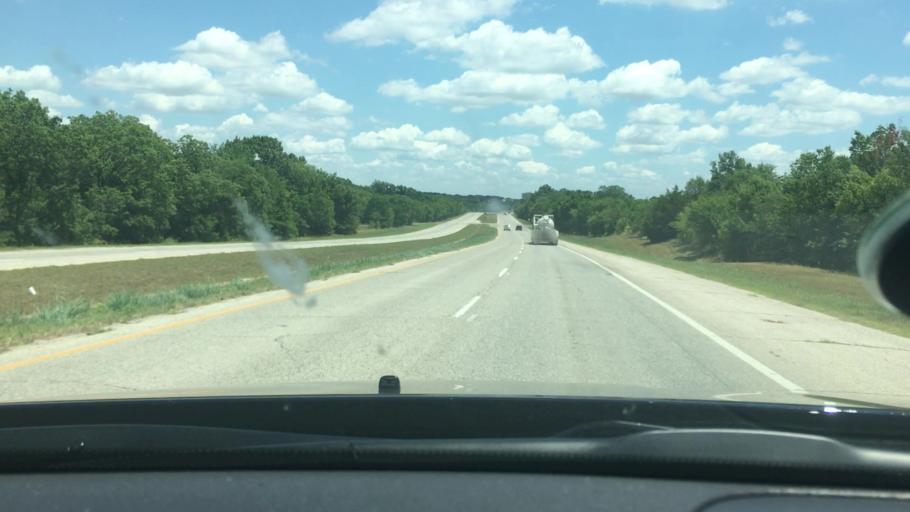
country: US
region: Oklahoma
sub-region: Carter County
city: Wilson
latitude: 34.1729
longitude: -97.3800
